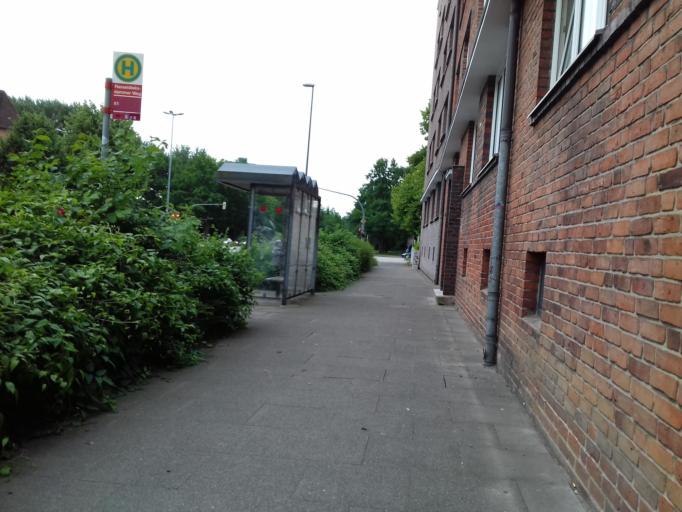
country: DE
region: Schleswig-Holstein
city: Kiel
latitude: 54.3216
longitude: 10.1113
